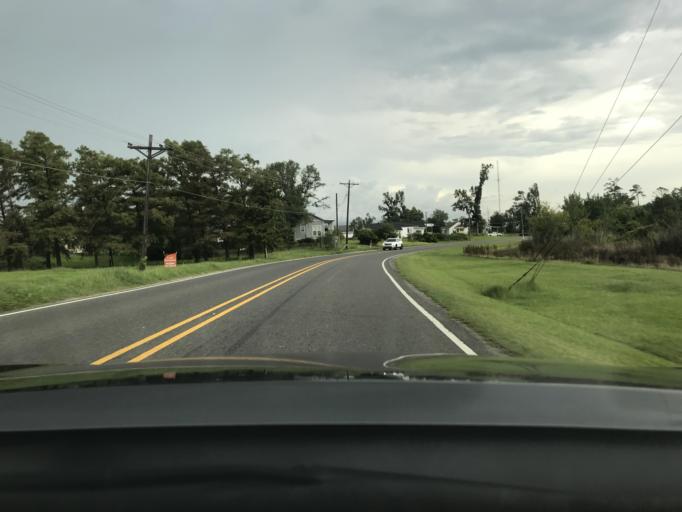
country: US
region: Louisiana
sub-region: Calcasieu Parish
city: Westlake
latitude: 30.2458
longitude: -93.2515
